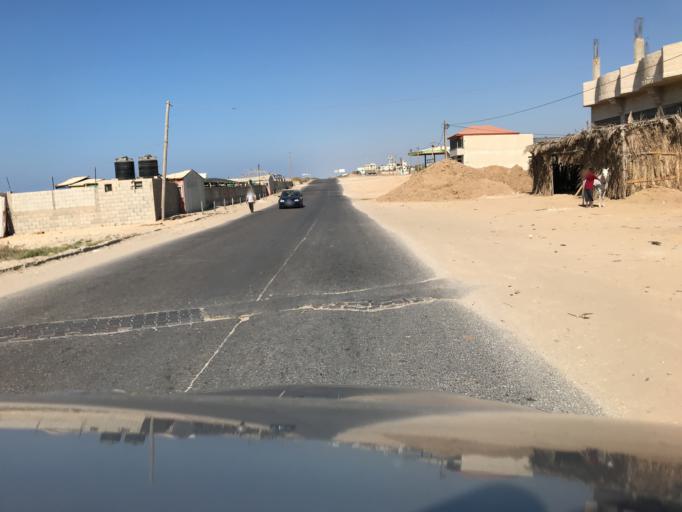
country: PS
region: Gaza Strip
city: Dayr al Balah
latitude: 31.4334
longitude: 34.3465
